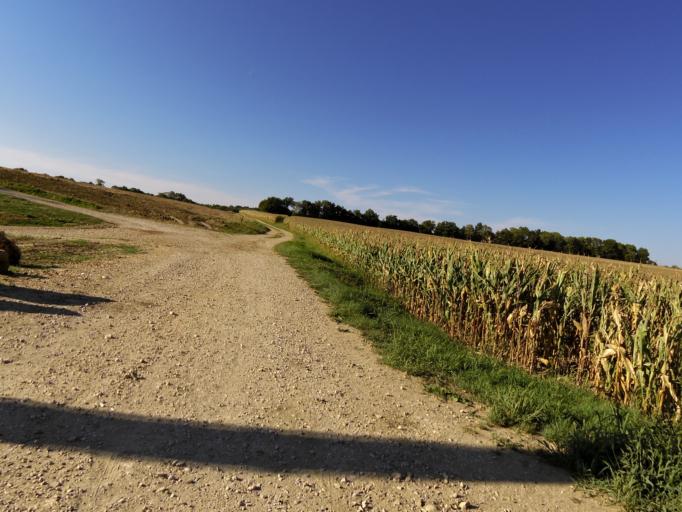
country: FR
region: Rhone-Alpes
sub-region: Departement de l'Ain
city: Perouges
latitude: 45.9379
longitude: 5.1687
